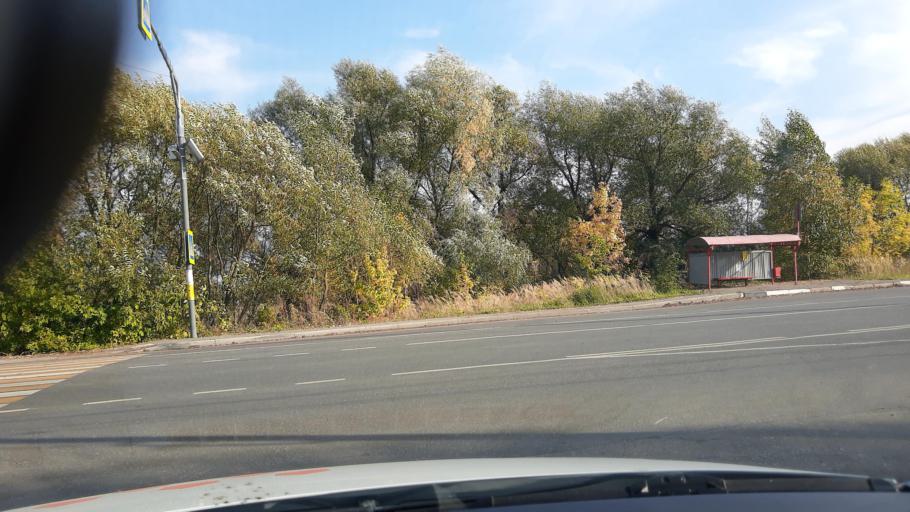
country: RU
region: Moskovskaya
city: Fryazevo
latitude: 55.7249
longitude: 38.4650
